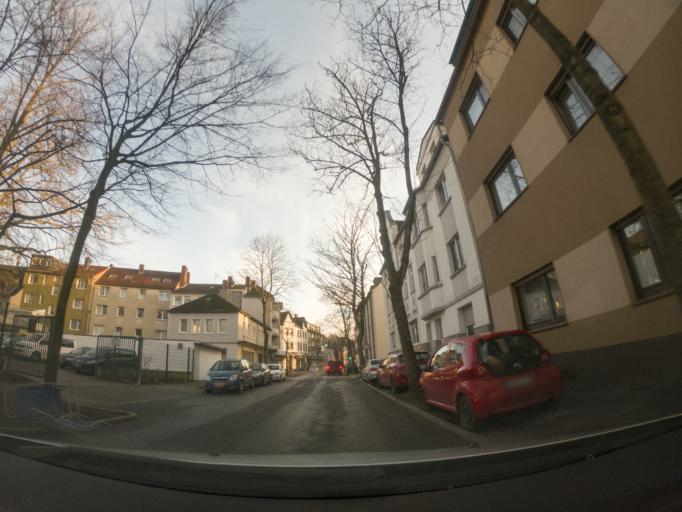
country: DE
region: North Rhine-Westphalia
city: Waltrop
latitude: 51.5968
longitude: 7.4435
